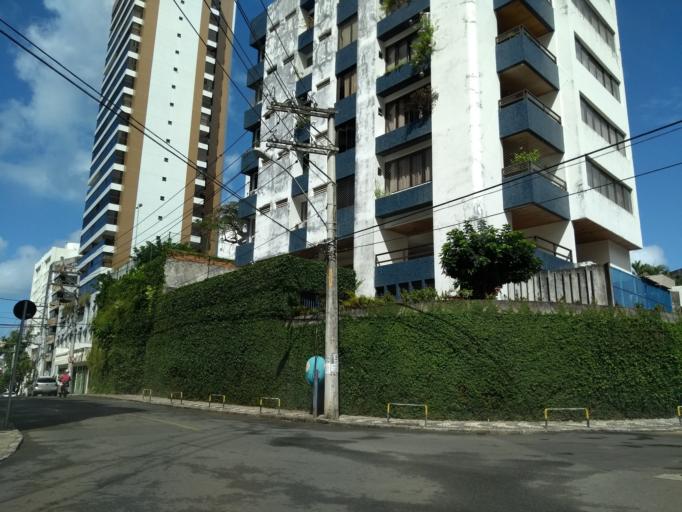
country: BR
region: Bahia
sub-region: Salvador
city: Salvador
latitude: -13.0038
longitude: -38.5210
